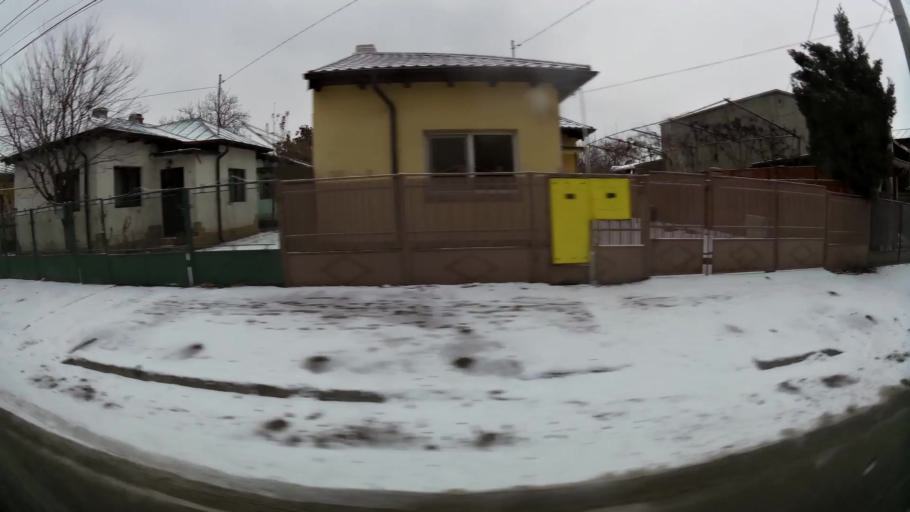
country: RO
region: Prahova
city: Ploiesti
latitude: 44.9306
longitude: 26.0393
